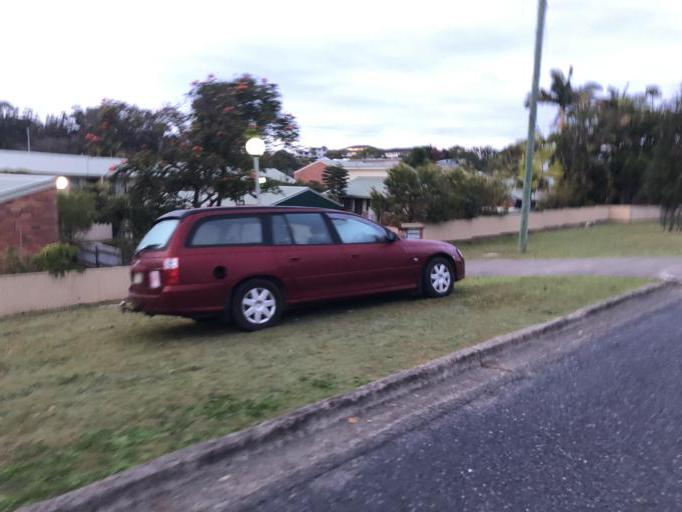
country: AU
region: New South Wales
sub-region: Coffs Harbour
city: Coffs Harbour
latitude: -30.3022
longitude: 153.1254
